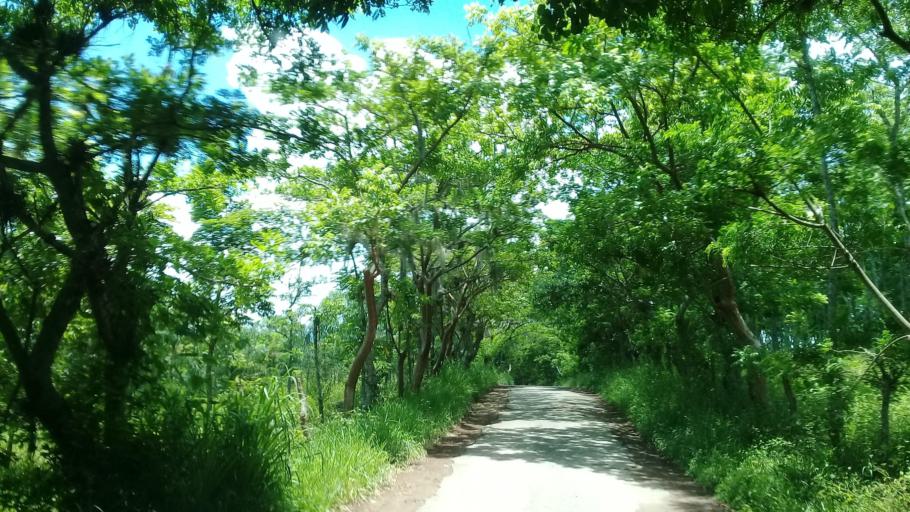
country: MX
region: Veracruz
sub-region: Naolinco
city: El Espinal
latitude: 19.5919
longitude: -96.8739
